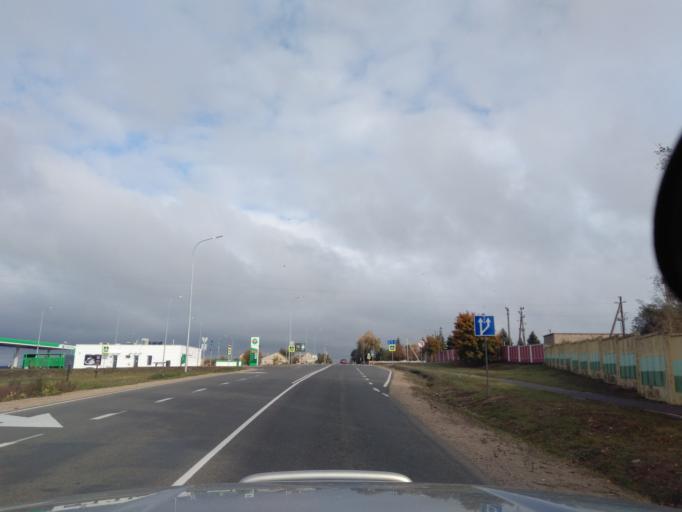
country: BY
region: Minsk
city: Kapyl'
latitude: 53.1479
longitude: 27.0750
